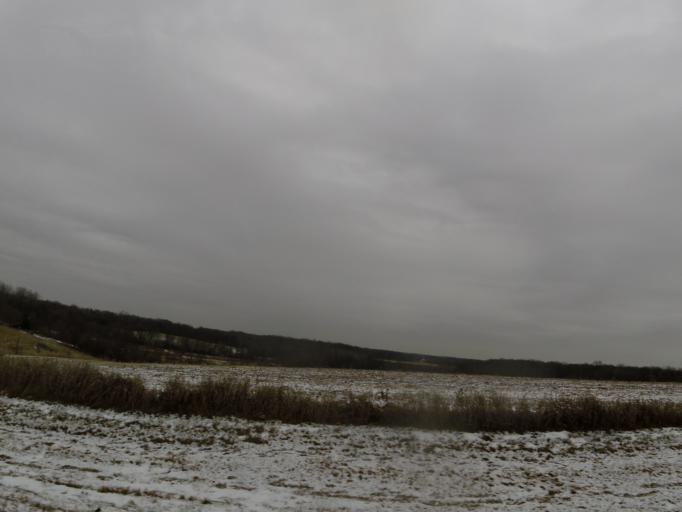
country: US
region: Minnesota
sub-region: Hennepin County
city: Medina
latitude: 45.0392
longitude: -93.5784
